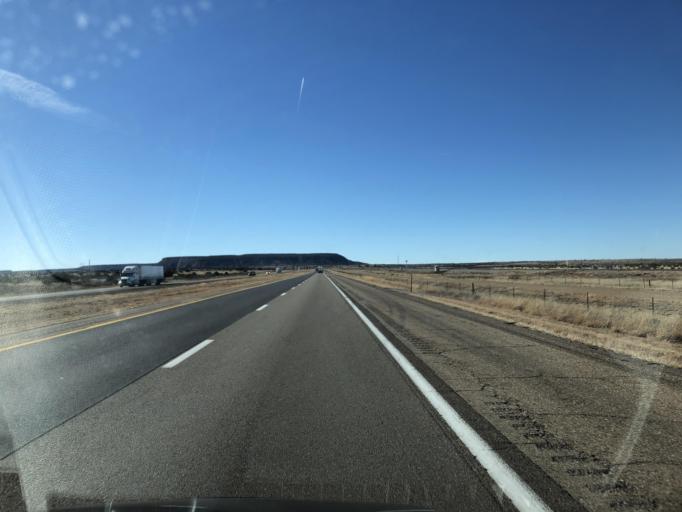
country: US
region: New Mexico
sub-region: Guadalupe County
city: Santa Rosa
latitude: 35.0579
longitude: -104.3185
